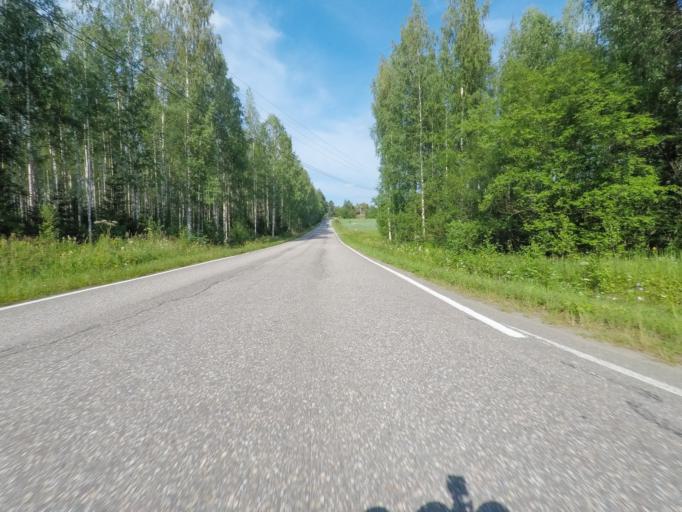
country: FI
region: Southern Savonia
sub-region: Savonlinna
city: Sulkava
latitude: 61.7595
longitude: 28.2300
